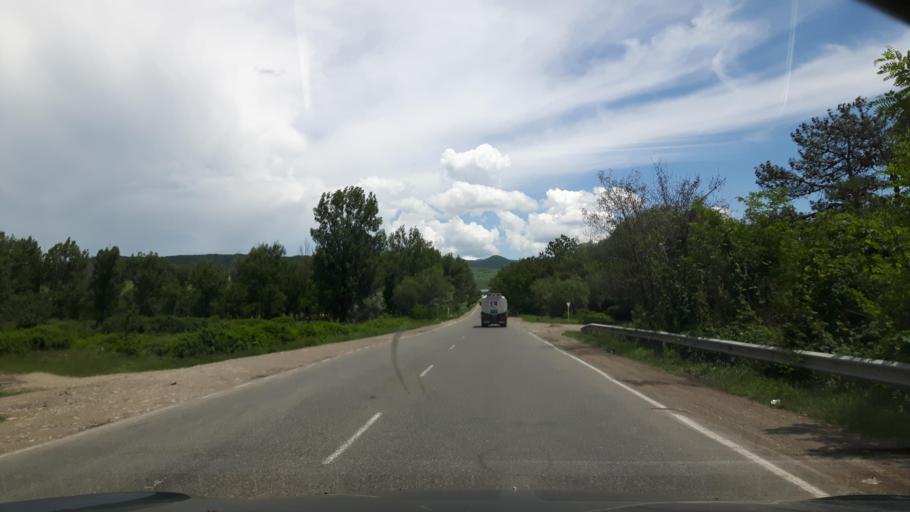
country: GE
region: Kakheti
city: Sagarejo
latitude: 41.7251
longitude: 45.1847
